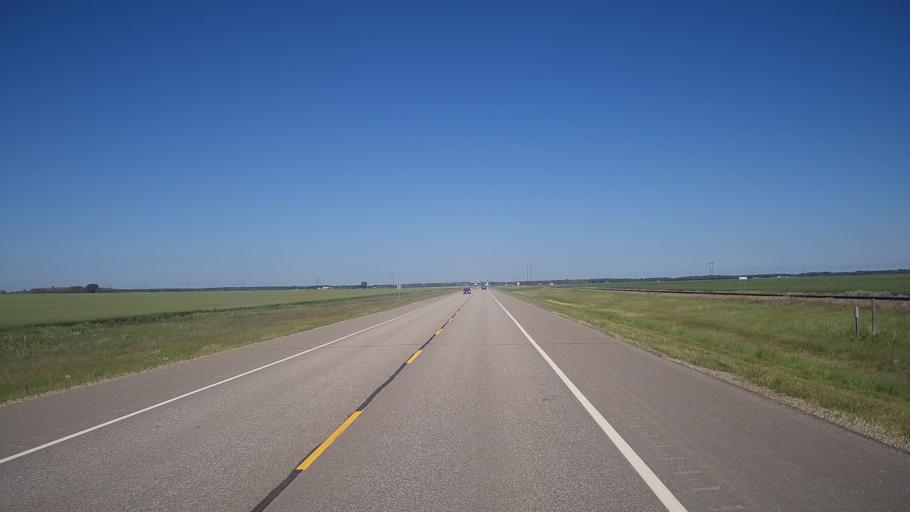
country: CA
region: Manitoba
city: Portage la Prairie
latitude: 50.1087
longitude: -98.5454
